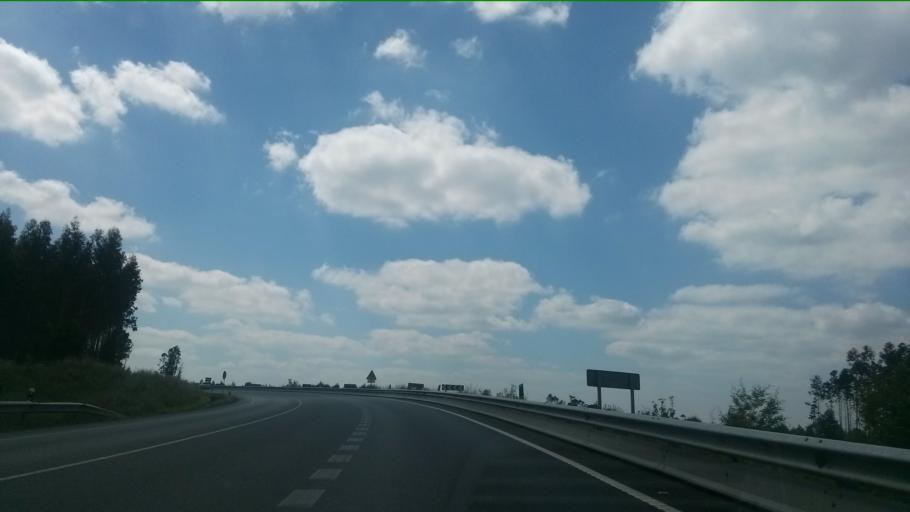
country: ES
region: Galicia
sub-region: Provincia da Coruna
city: Frades
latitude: 42.9991
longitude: -8.2753
